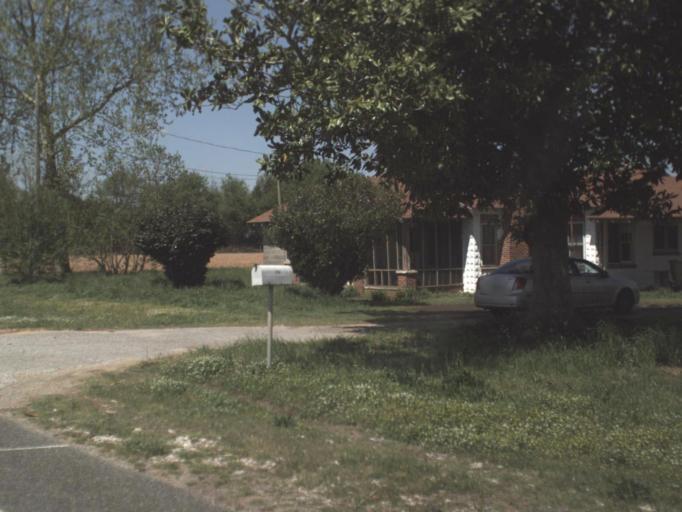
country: US
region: Florida
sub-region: Escambia County
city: Century
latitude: 30.9516
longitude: -87.1664
